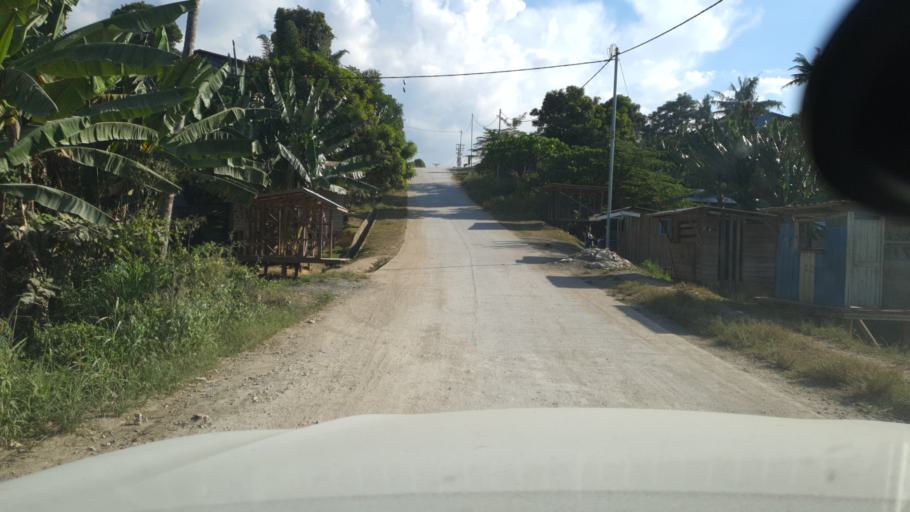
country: SB
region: Guadalcanal
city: Honiara
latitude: -9.4460
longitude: 159.9975
